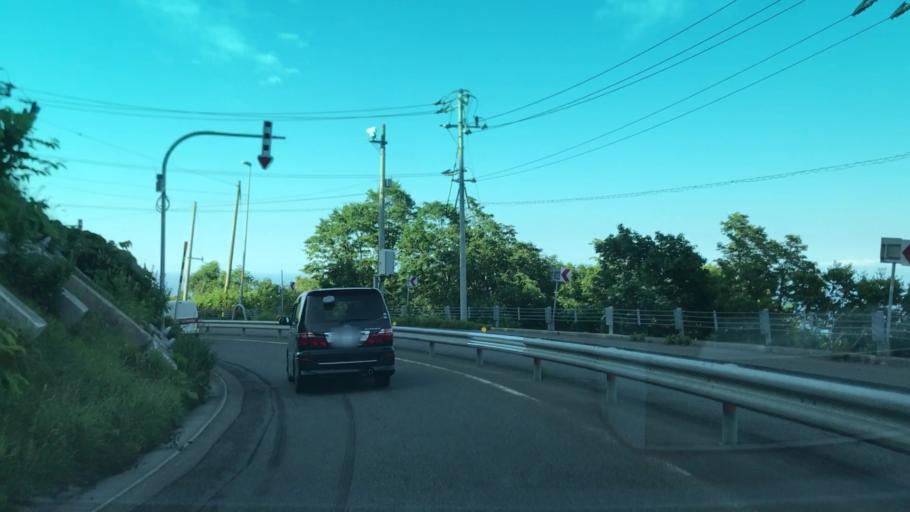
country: JP
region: Hokkaido
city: Otaru
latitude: 43.1394
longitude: 141.0148
